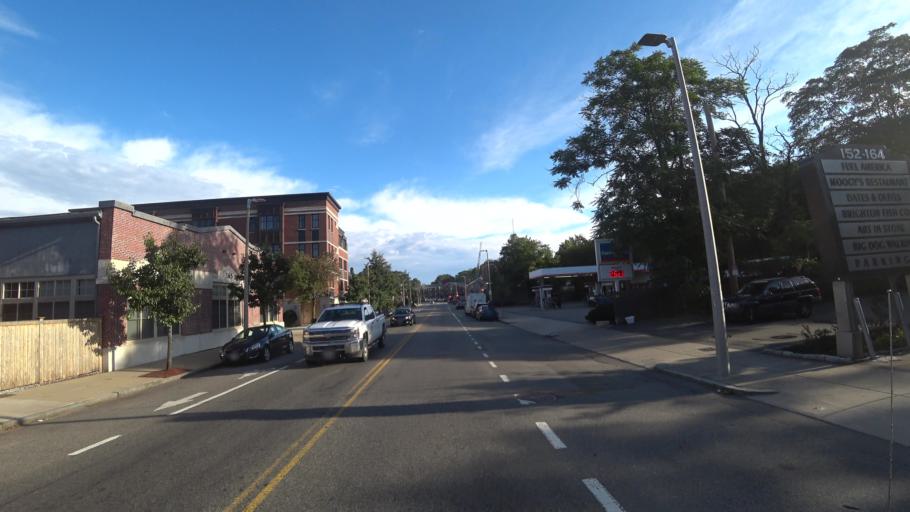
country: US
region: Massachusetts
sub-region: Norfolk County
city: Brookline
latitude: 42.3418
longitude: -71.1544
